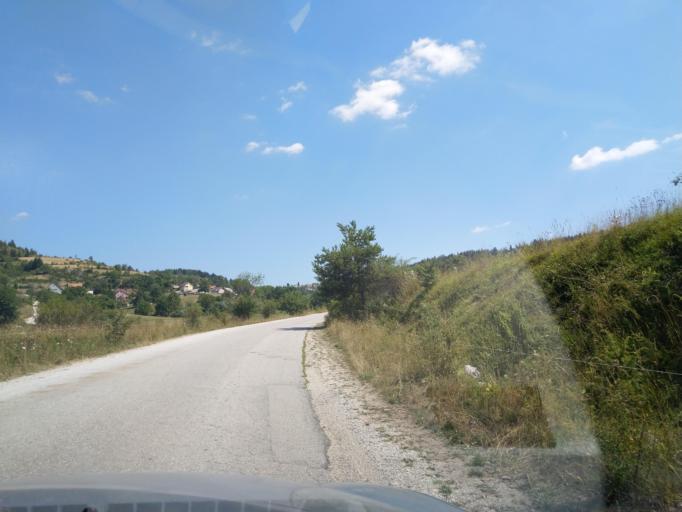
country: RS
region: Central Serbia
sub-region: Zlatiborski Okrug
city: Nova Varos
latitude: 43.4517
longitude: 19.9682
